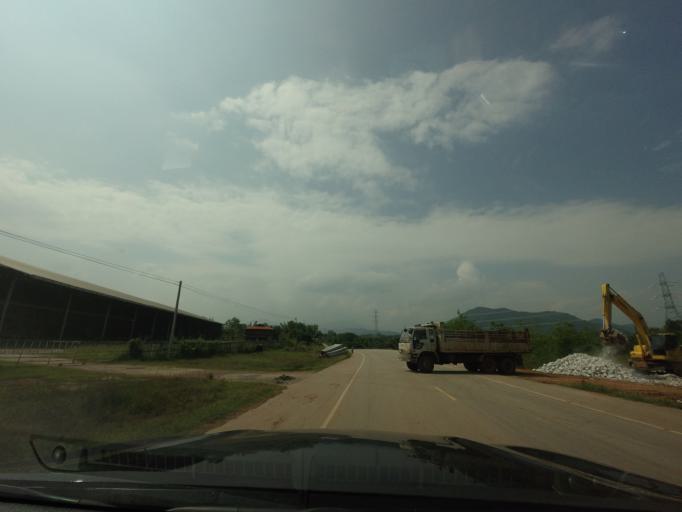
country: LA
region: Xiagnabouli
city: Muang Kenthao
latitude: 17.6879
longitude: 101.4112
